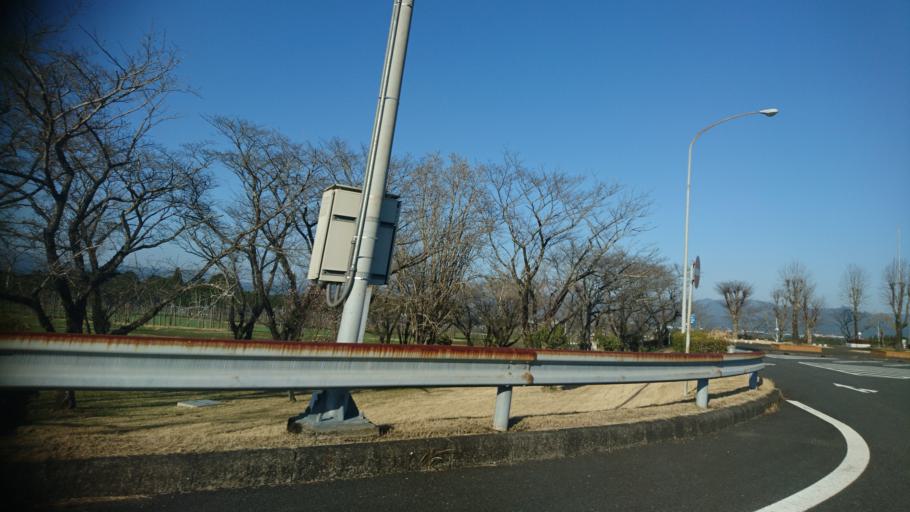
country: JP
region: Miyazaki
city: Kobayashi
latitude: 31.9684
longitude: 130.9531
